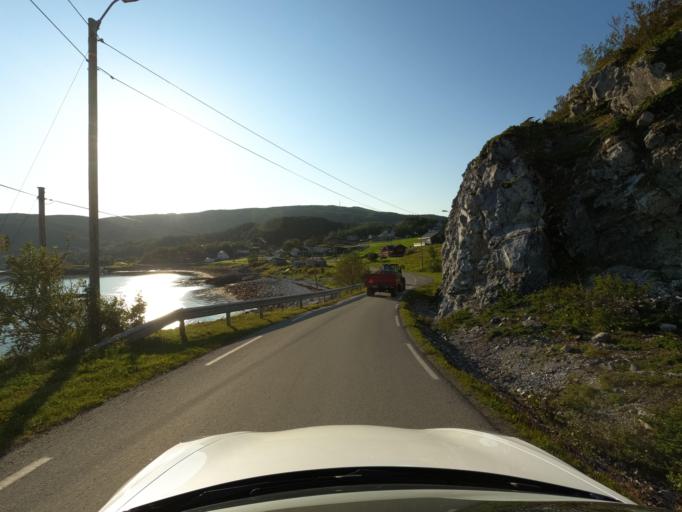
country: NO
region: Troms
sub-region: Skanland
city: Evenskjer
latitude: 68.4550
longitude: 16.6059
